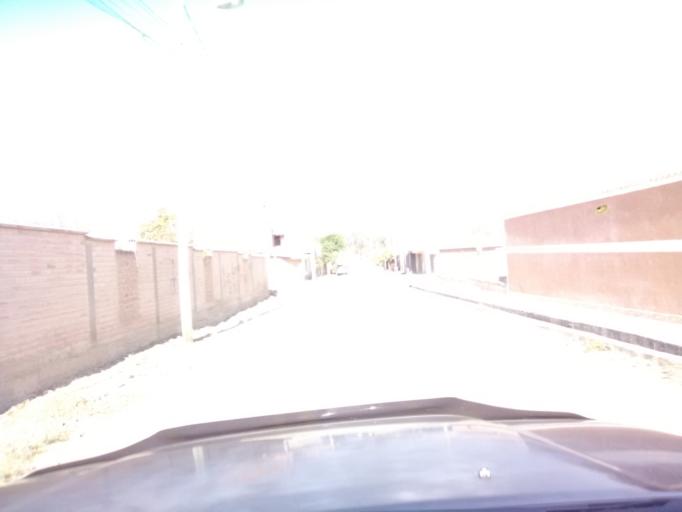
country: BO
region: Cochabamba
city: Cochabamba
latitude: -17.3602
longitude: -66.2072
